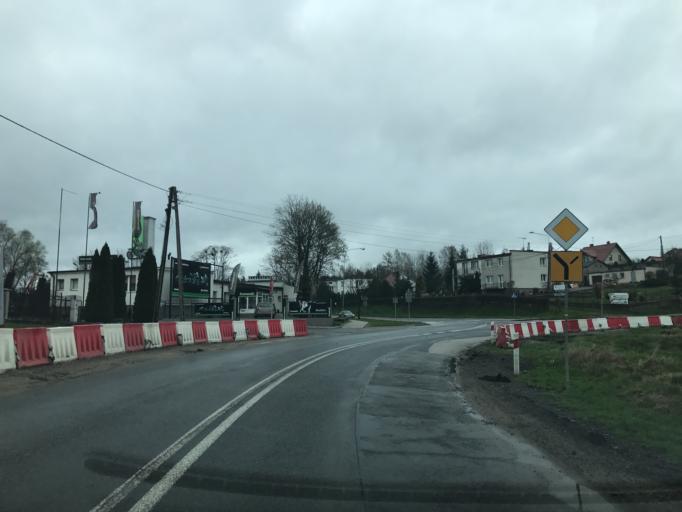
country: PL
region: Warmian-Masurian Voivodeship
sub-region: Powiat ostrodzki
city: Ostroda
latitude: 53.7058
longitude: 19.9791
